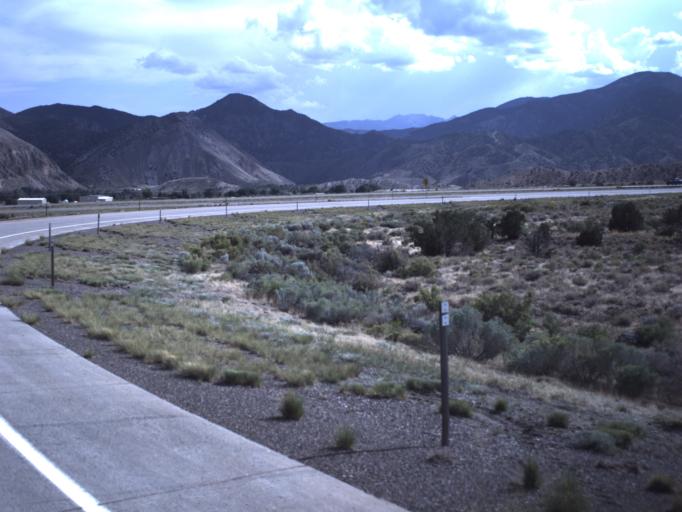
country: US
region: Utah
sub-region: Sevier County
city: Monroe
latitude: 38.6019
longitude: -112.2519
